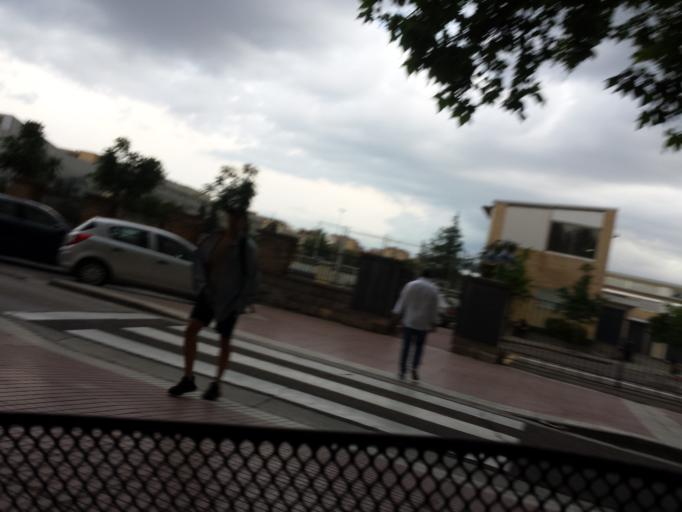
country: ES
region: Aragon
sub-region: Provincia de Zaragoza
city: Delicias
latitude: 41.6446
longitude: -0.9002
